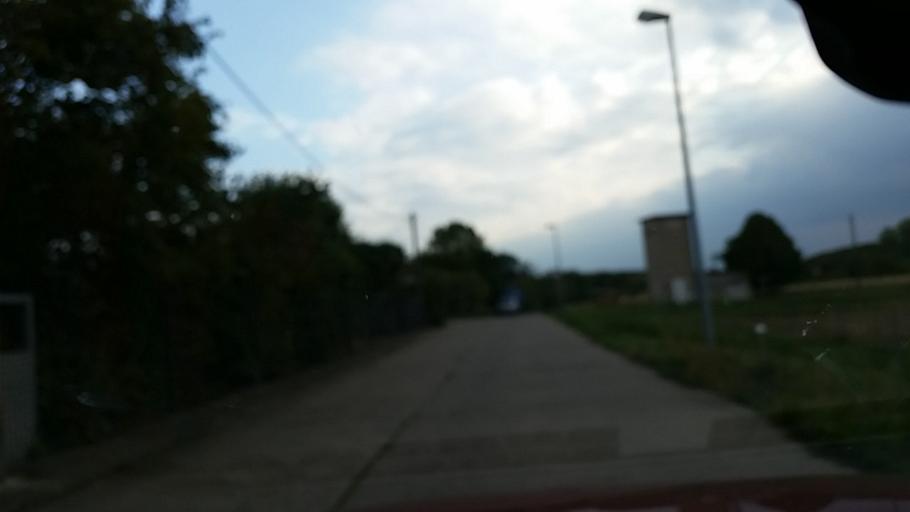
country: DE
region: Thuringia
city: Beichlingen
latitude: 51.2310
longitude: 11.2528
